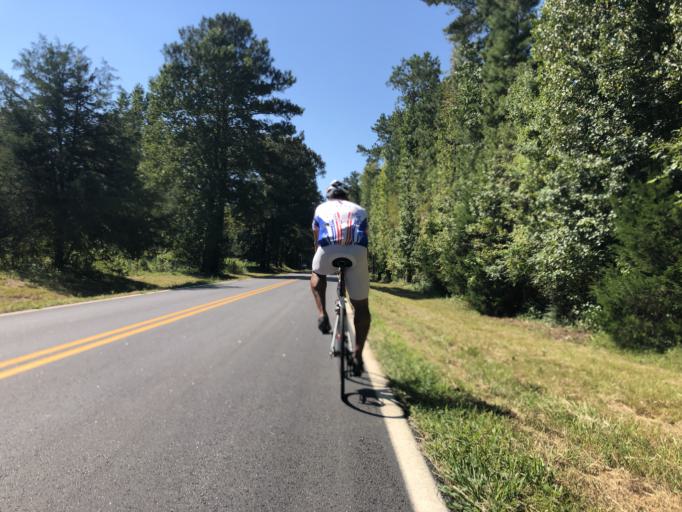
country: US
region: Georgia
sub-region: Heard County
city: Franklin
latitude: 33.3789
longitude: -84.9691
